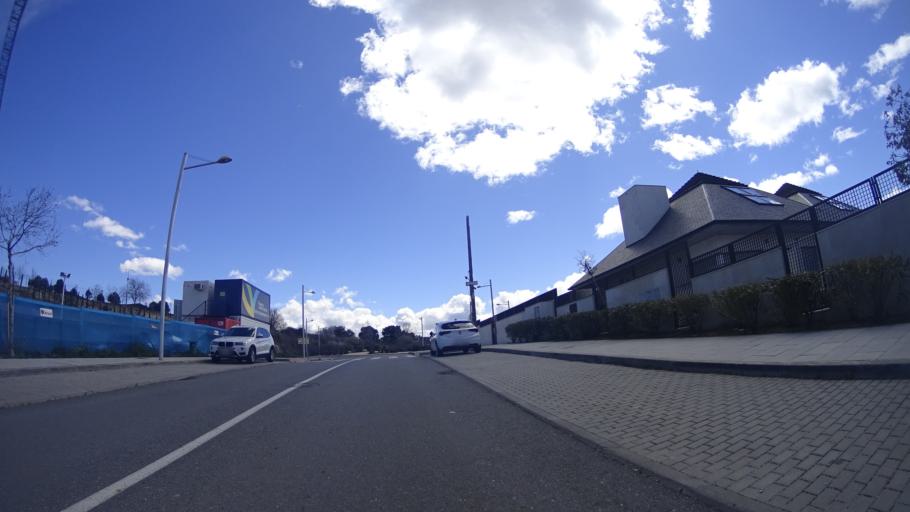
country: ES
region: Madrid
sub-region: Provincia de Madrid
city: Torrelodones
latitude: 40.5644
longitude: -3.9167
